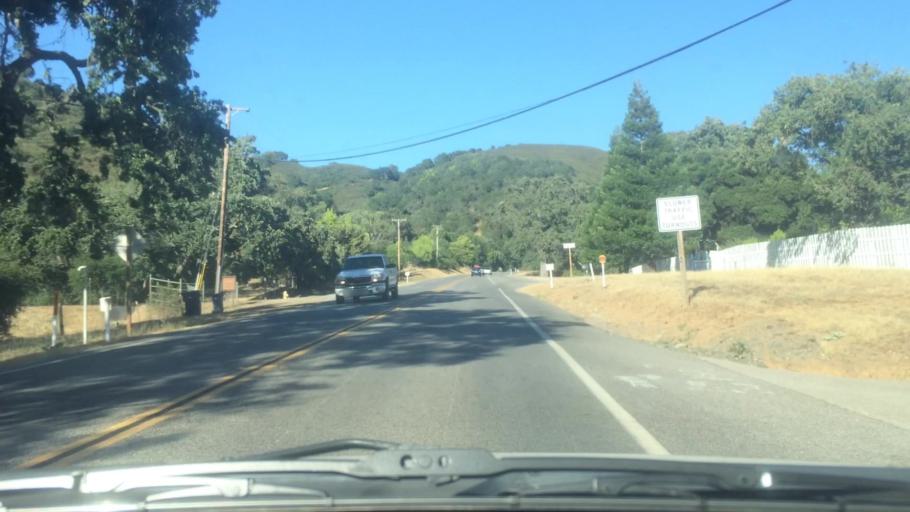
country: US
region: California
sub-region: San Luis Obispo County
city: Atascadero
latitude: 35.4591
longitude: -120.7237
